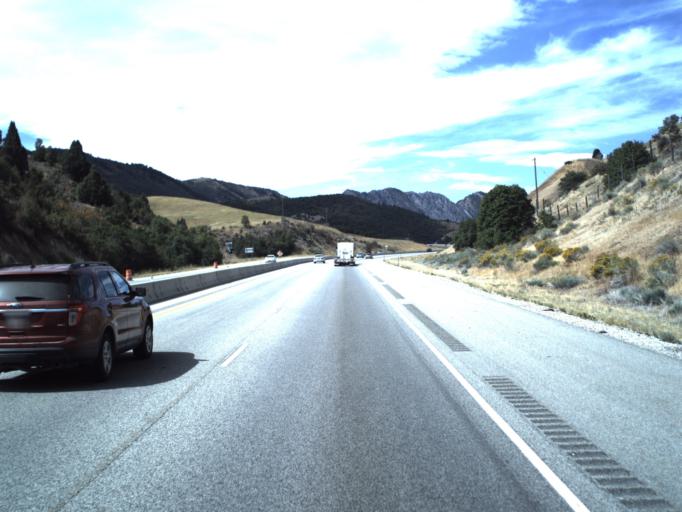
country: US
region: Utah
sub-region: Box Elder County
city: Brigham City
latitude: 41.5210
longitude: -111.9433
